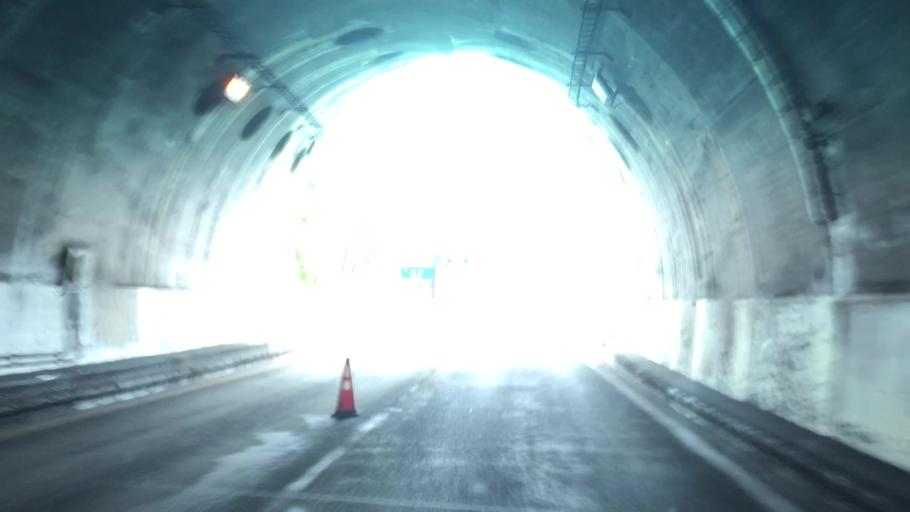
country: JP
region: Hokkaido
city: Otaru
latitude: 43.1685
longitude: 141.0432
